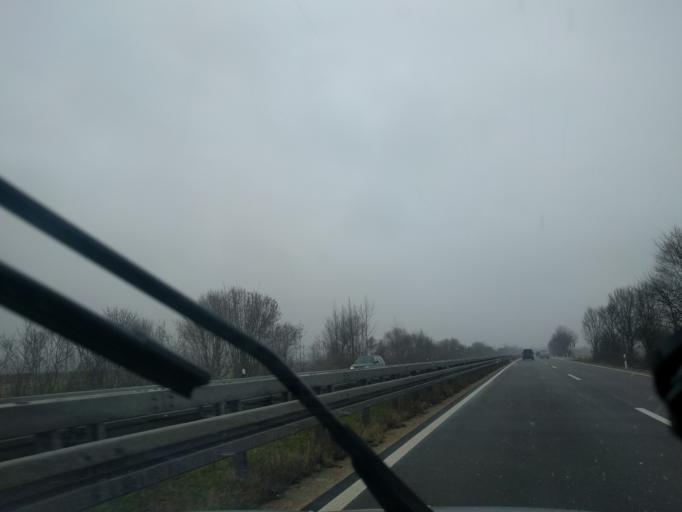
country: DE
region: Bavaria
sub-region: Swabia
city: Nordendorf
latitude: 48.6243
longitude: 10.8364
